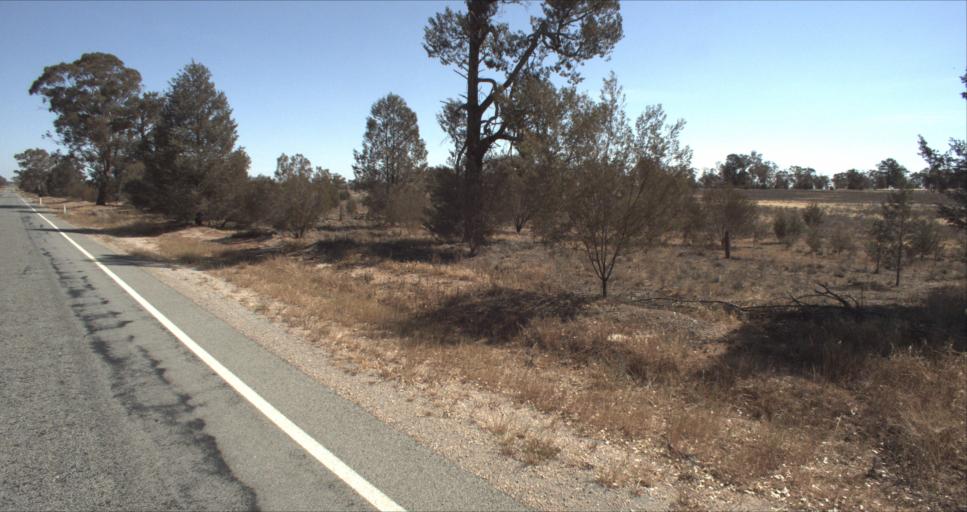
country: AU
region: New South Wales
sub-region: Leeton
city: Leeton
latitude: -34.4819
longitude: 146.4340
